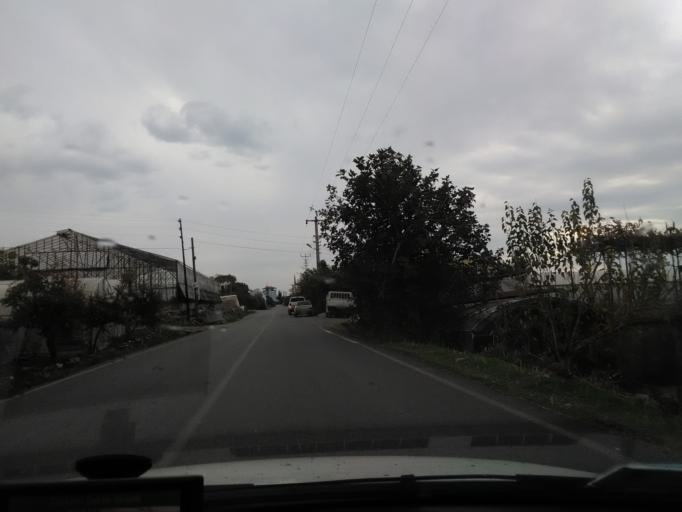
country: TR
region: Antalya
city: Gazipasa
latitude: 36.2561
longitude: 32.3053
